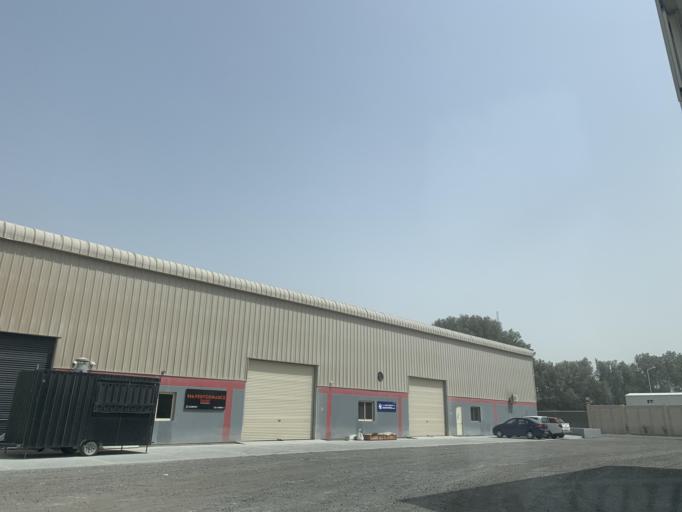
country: BH
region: Northern
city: Madinat `Isa
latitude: 26.1891
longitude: 50.5287
